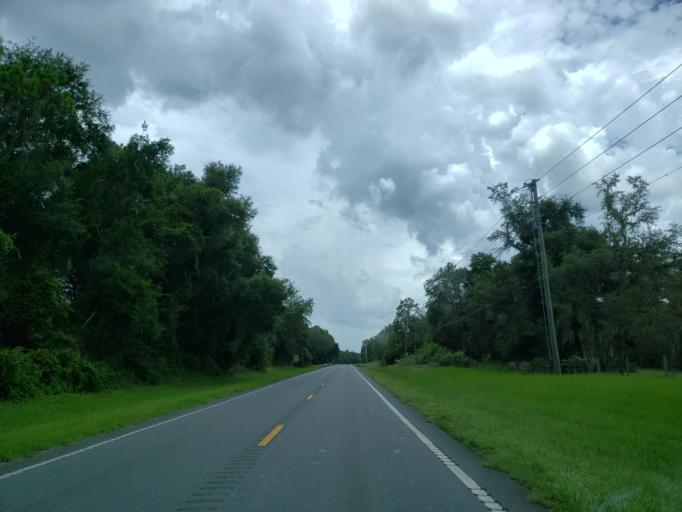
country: US
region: Florida
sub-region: Sumter County
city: Bushnell
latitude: 28.6401
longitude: -82.2351
